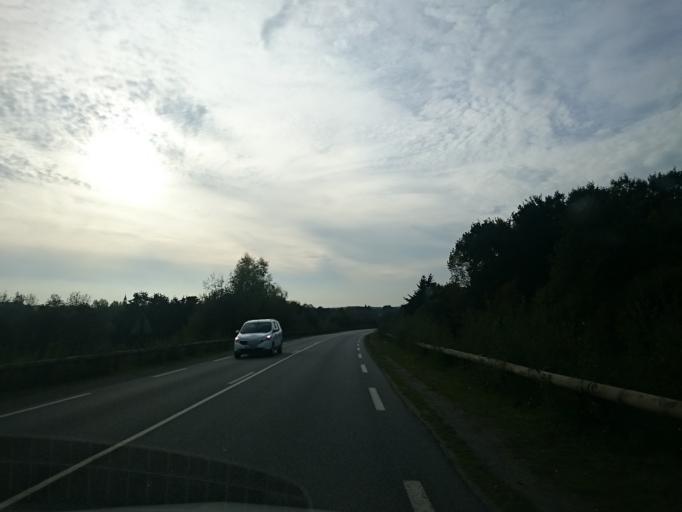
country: FR
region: Brittany
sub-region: Departement d'Ille-et-Vilaine
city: Bourgbarre
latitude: 47.9988
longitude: -1.6062
